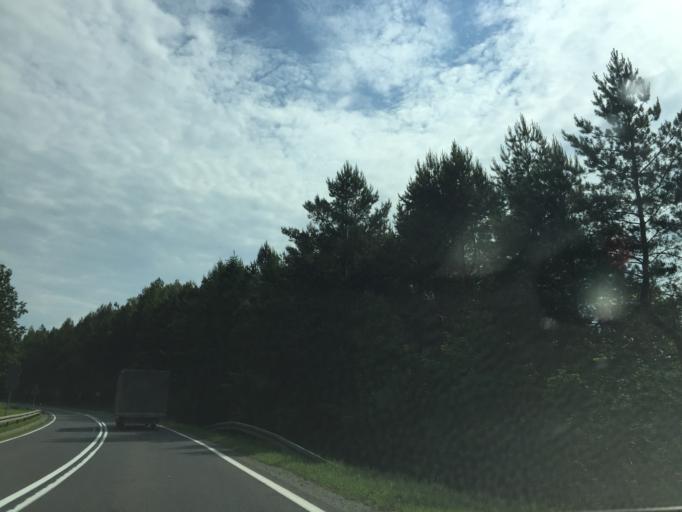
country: PL
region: Warmian-Masurian Voivodeship
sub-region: Powiat olsztynski
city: Gietrzwald
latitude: 53.7135
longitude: 20.1289
